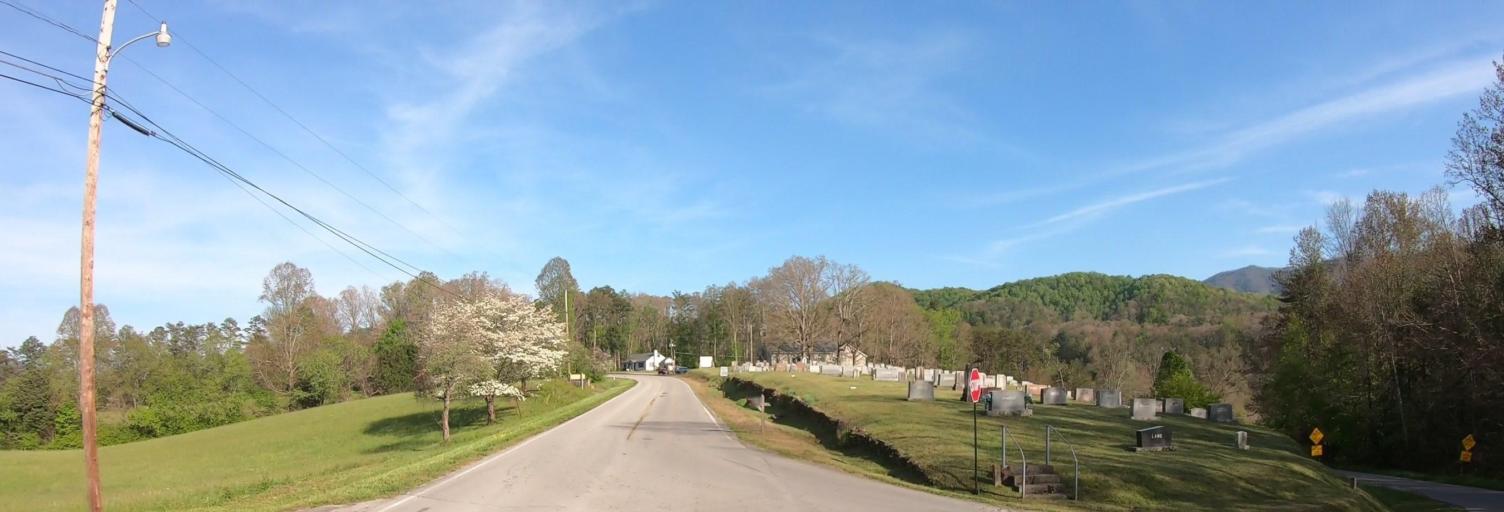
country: US
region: Tennessee
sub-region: Blount County
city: Wildwood
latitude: 35.6734
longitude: -83.7781
